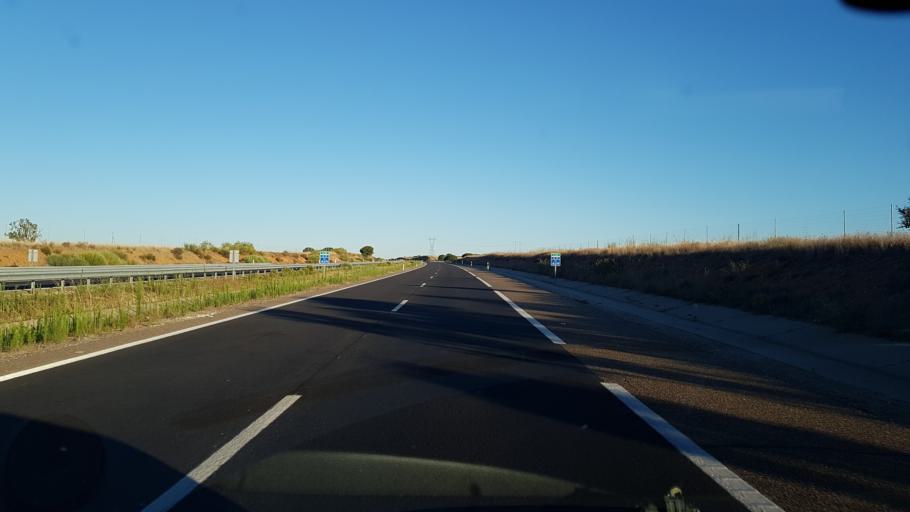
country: ES
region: Castille and Leon
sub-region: Provincia de Zamora
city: Toro
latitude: 41.5447
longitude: -5.4210
